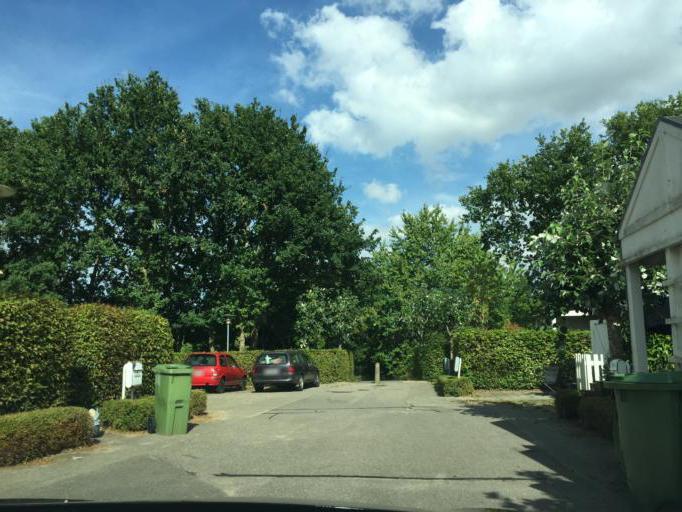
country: DK
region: South Denmark
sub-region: Odense Kommune
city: Hojby
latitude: 55.3464
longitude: 10.3898
